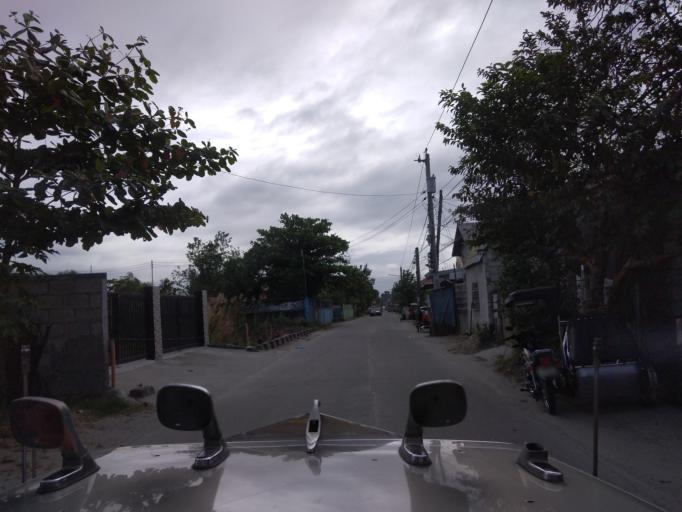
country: PH
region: Central Luzon
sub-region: Province of Pampanga
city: Mexico
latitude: 15.0696
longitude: 120.7149
